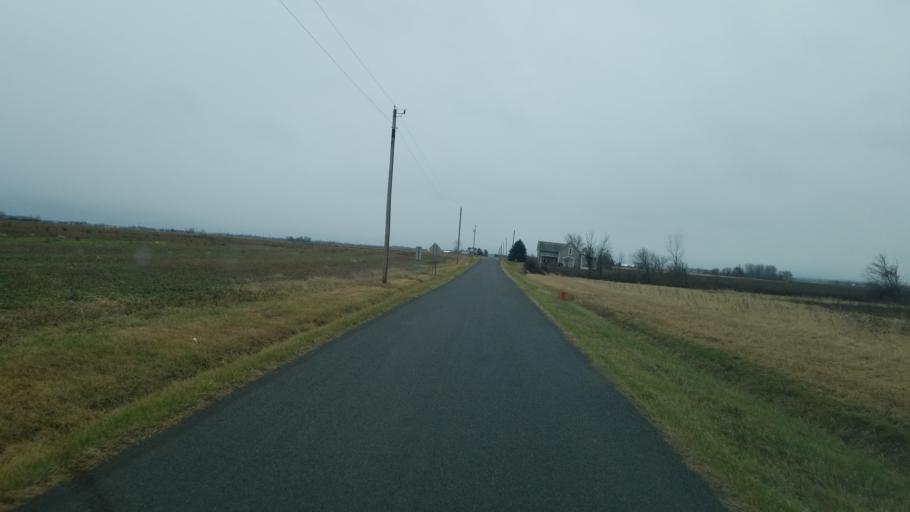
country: US
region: Ohio
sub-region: Logan County
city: Northwood
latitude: 40.4508
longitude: -83.5659
